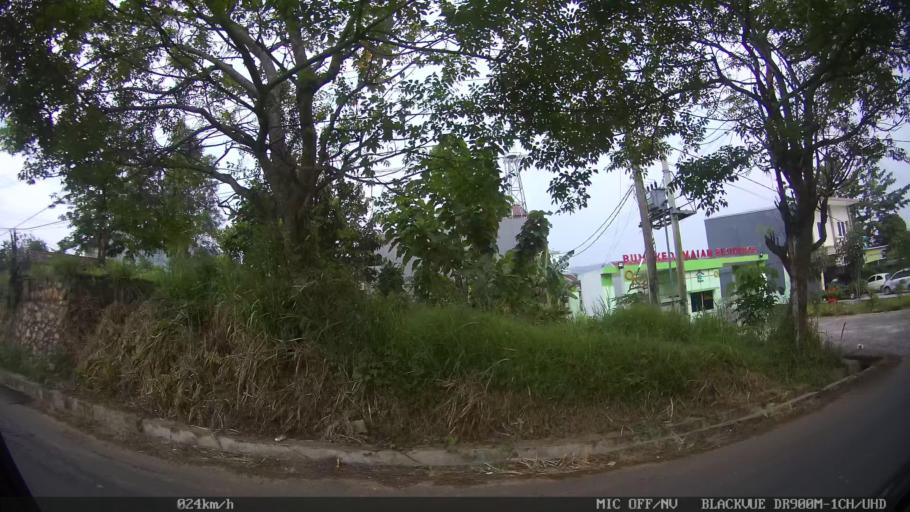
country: ID
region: Lampung
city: Bandarlampung
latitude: -5.4150
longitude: 105.2849
